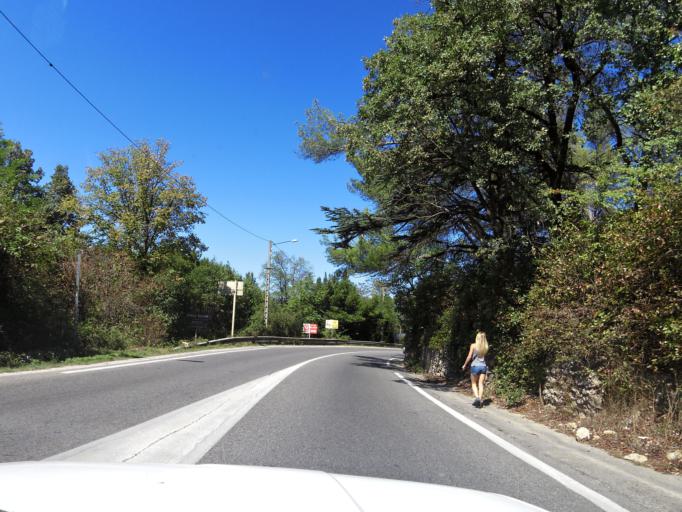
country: FR
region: Languedoc-Roussillon
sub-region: Departement du Gard
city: Saint-Christol-les-Ales
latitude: 44.1009
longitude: 4.0813
